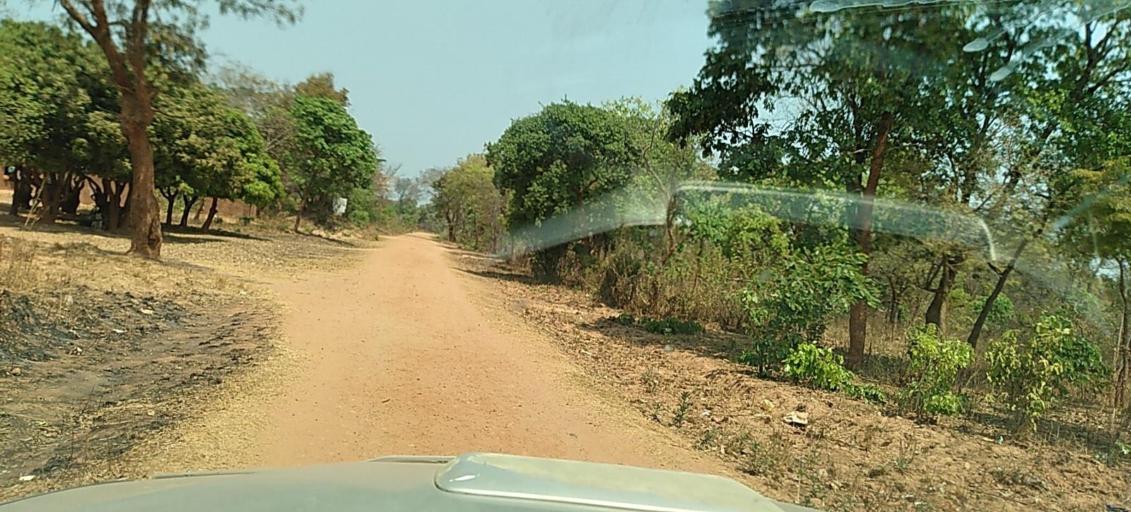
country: ZM
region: North-Western
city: Kasempa
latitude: -13.6987
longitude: 26.3294
